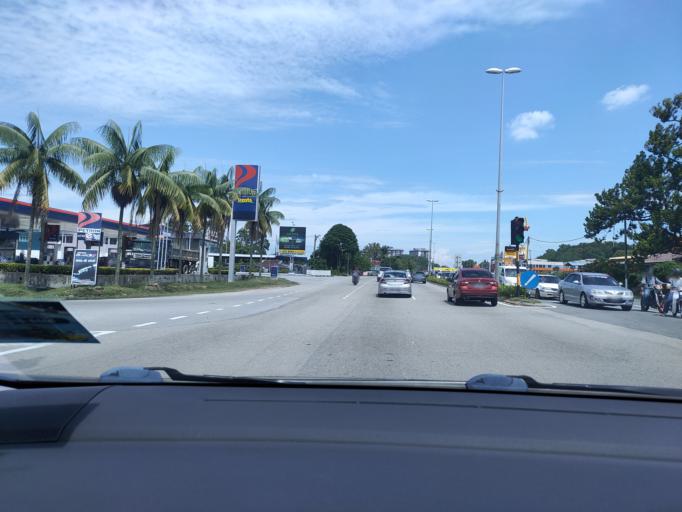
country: MY
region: Melaka
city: Batu Berendam
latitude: 2.2555
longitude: 102.2225
